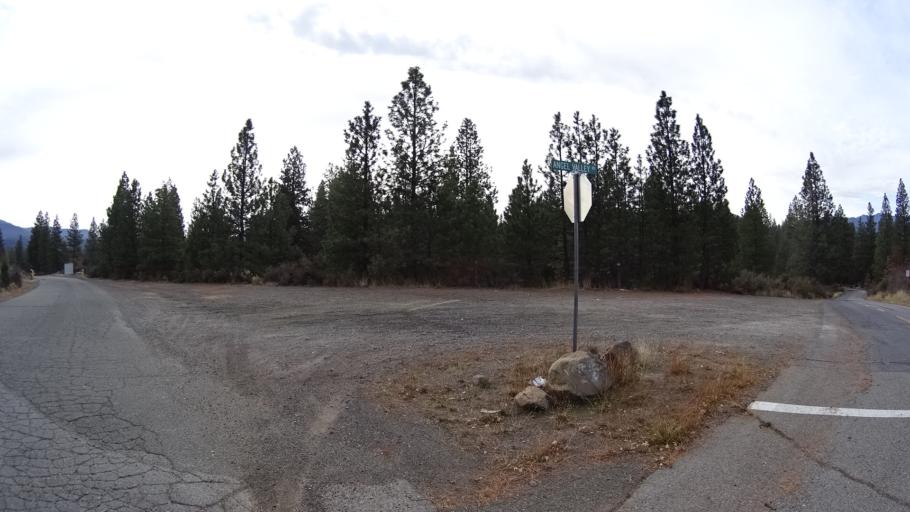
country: US
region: California
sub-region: Siskiyou County
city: Weed
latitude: 41.4431
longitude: -122.3725
